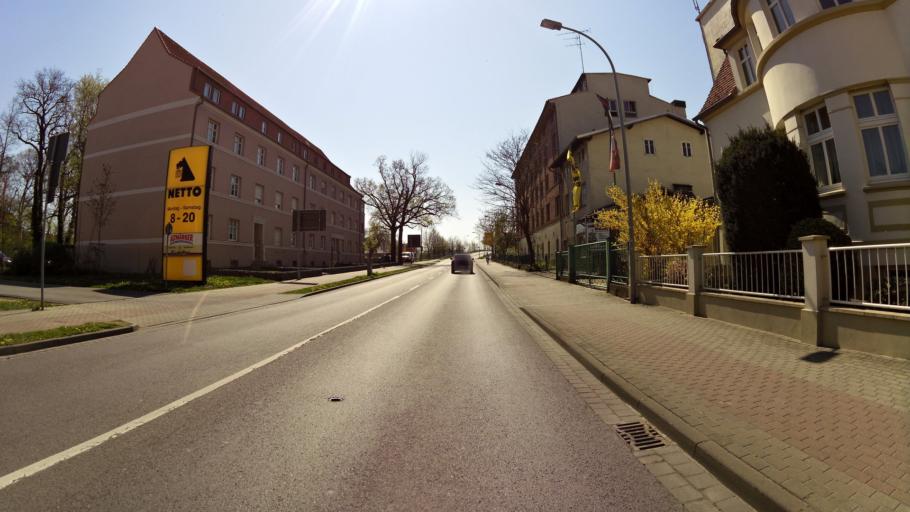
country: DE
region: Saxony-Anhalt
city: Stendal
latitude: 52.5983
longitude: 11.8650
